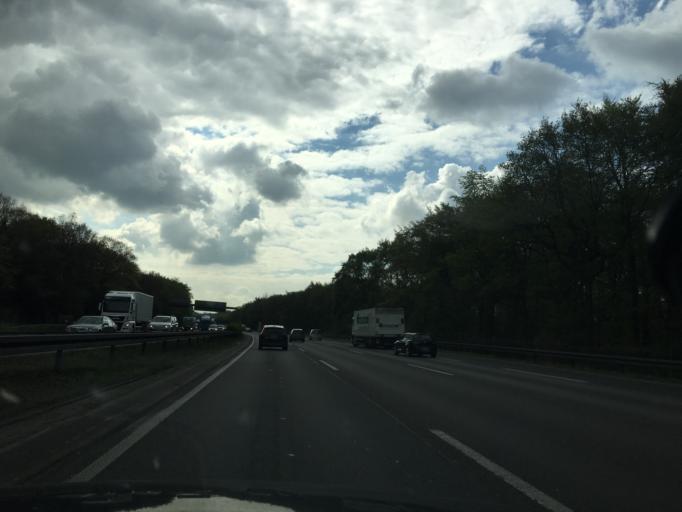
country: DE
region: North Rhine-Westphalia
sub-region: Regierungsbezirk Dusseldorf
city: Duisburg
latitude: 51.4060
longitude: 6.8034
